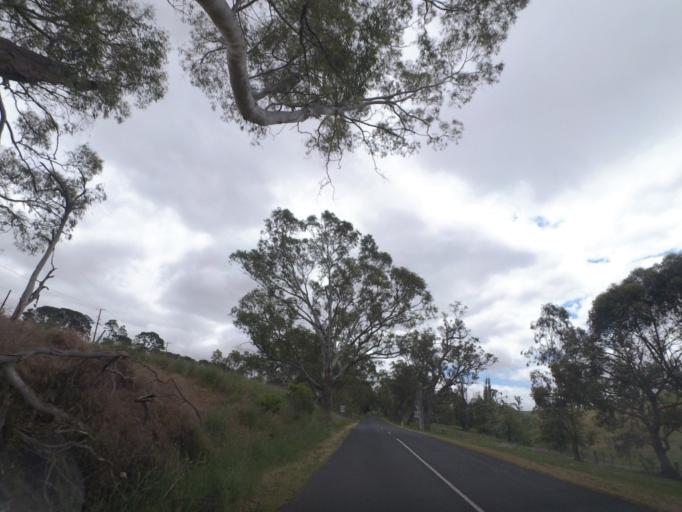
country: AU
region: Victoria
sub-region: Whittlesea
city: Whittlesea
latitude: -37.1971
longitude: 145.0381
